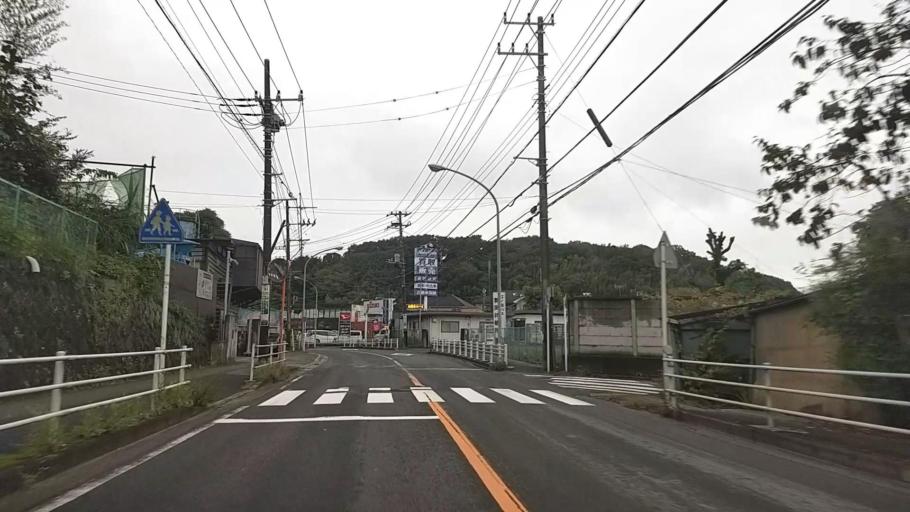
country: JP
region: Kanagawa
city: Kamakura
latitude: 35.4025
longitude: 139.5531
